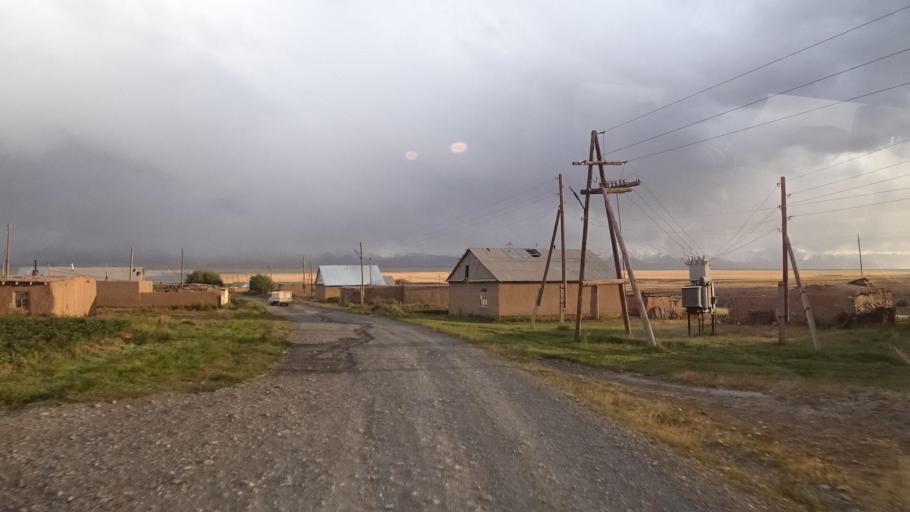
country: KG
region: Osh
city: Osh
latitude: 39.6645
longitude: 72.8845
